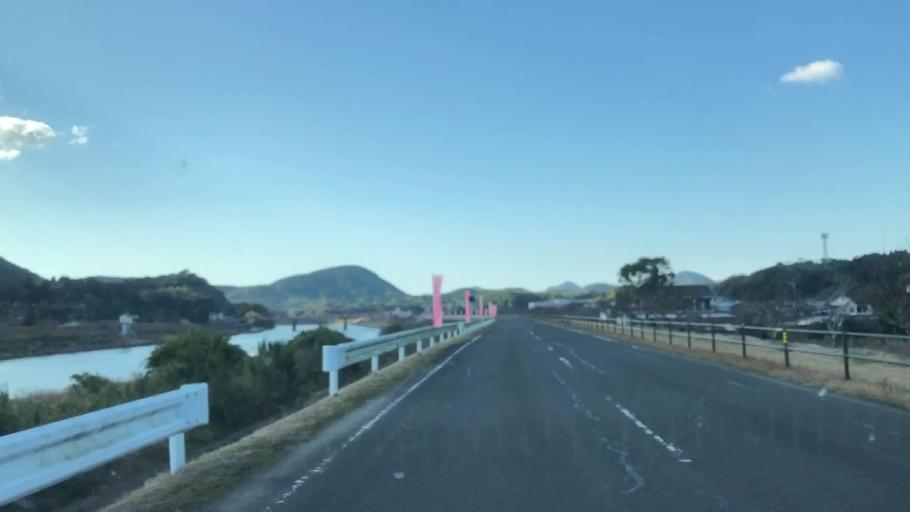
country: JP
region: Kagoshima
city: Satsumasendai
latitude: 31.8597
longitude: 130.3454
